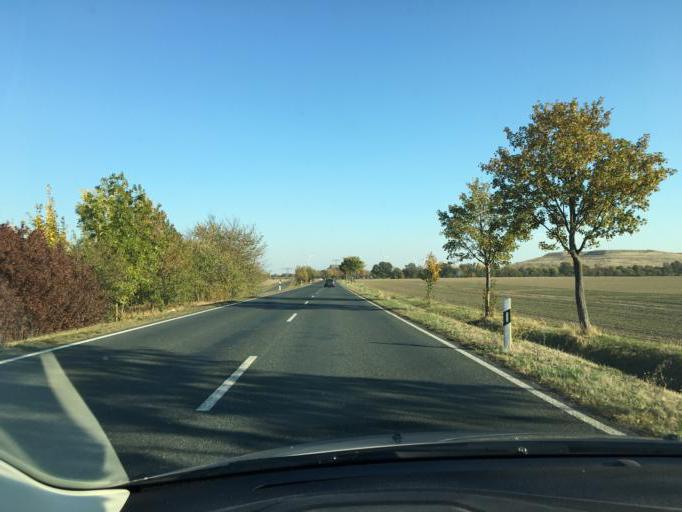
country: DE
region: Saxony
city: Rackwitz
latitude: 51.4197
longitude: 12.3879
